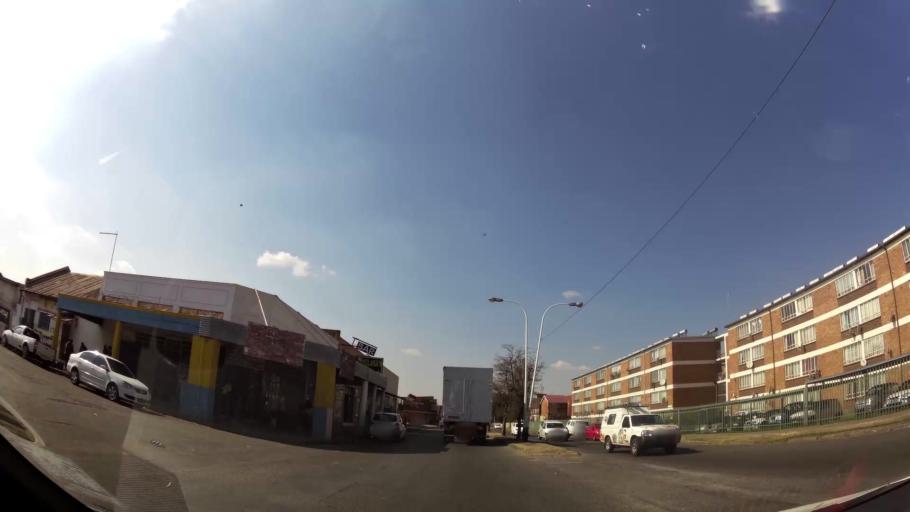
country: ZA
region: Gauteng
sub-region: Ekurhuleni Metropolitan Municipality
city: Boksburg
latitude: -26.2087
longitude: 28.2572
